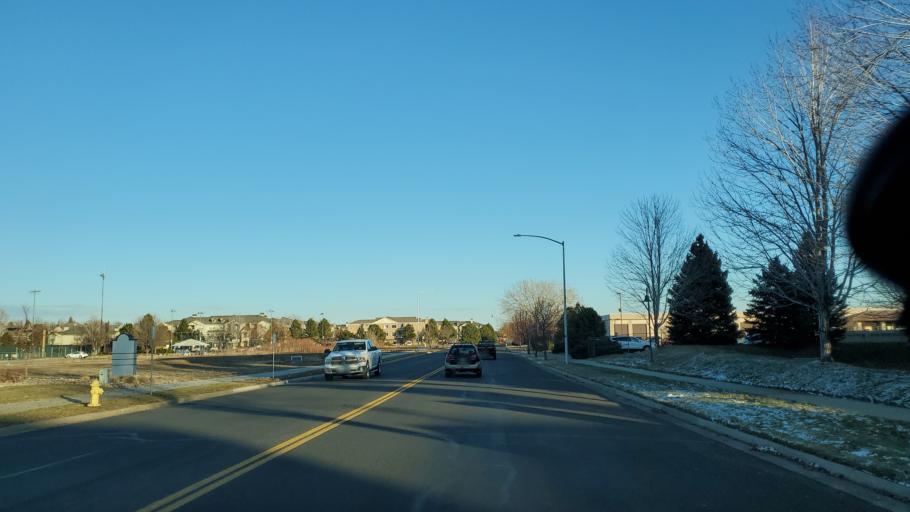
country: US
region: Colorado
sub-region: Broomfield County
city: Broomfield
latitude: 39.9160
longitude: -105.0654
